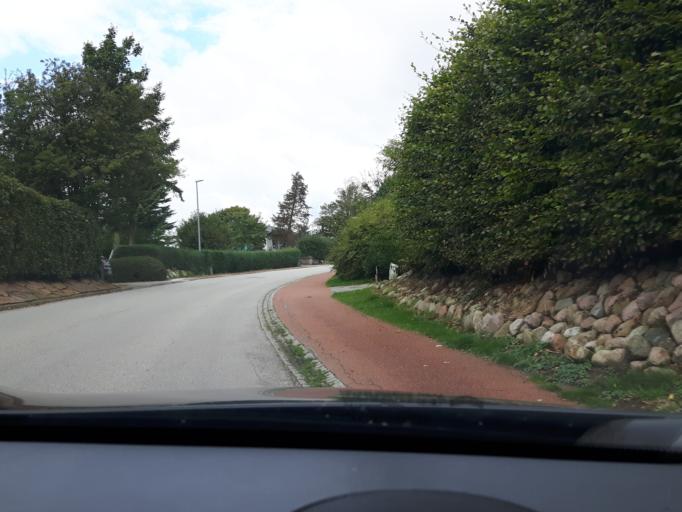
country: DK
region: Central Jutland
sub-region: Hedensted Kommune
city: Hornsyld
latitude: 55.7007
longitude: 9.7882
